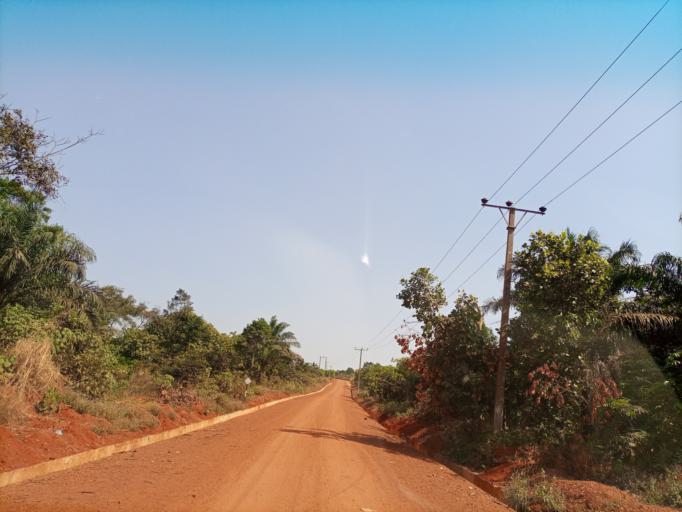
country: NG
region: Enugu
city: Nsukka
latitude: 6.8004
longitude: 7.3417
